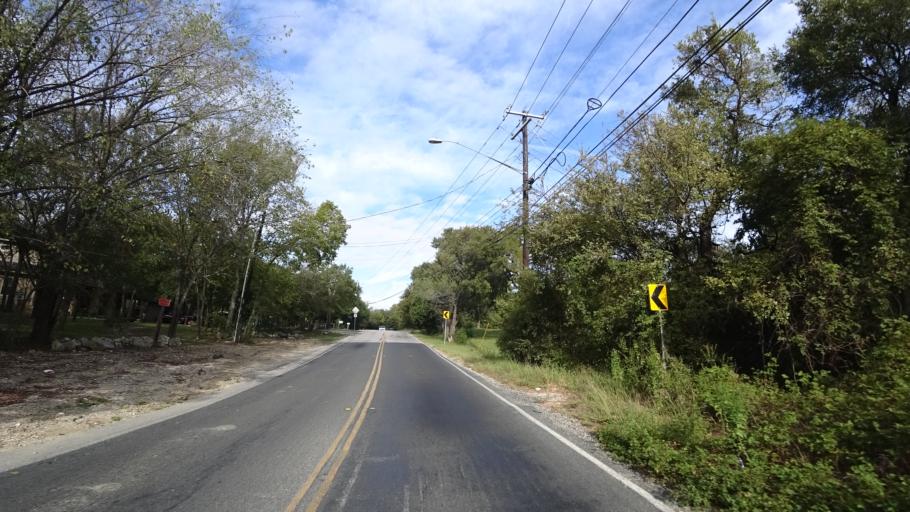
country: US
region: Texas
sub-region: Travis County
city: Austin
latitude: 30.2036
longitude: -97.7335
